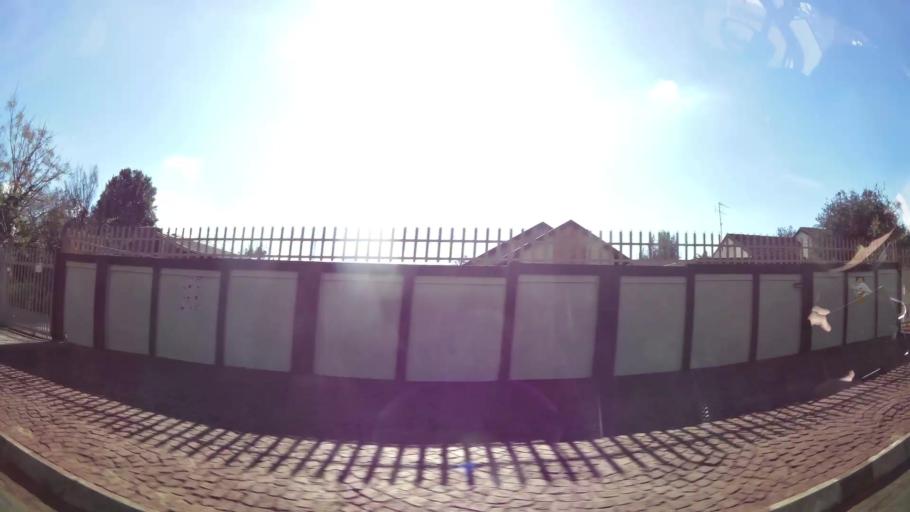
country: ZA
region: Gauteng
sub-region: City of Johannesburg Metropolitan Municipality
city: Roodepoort
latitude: -26.1488
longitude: 27.8263
